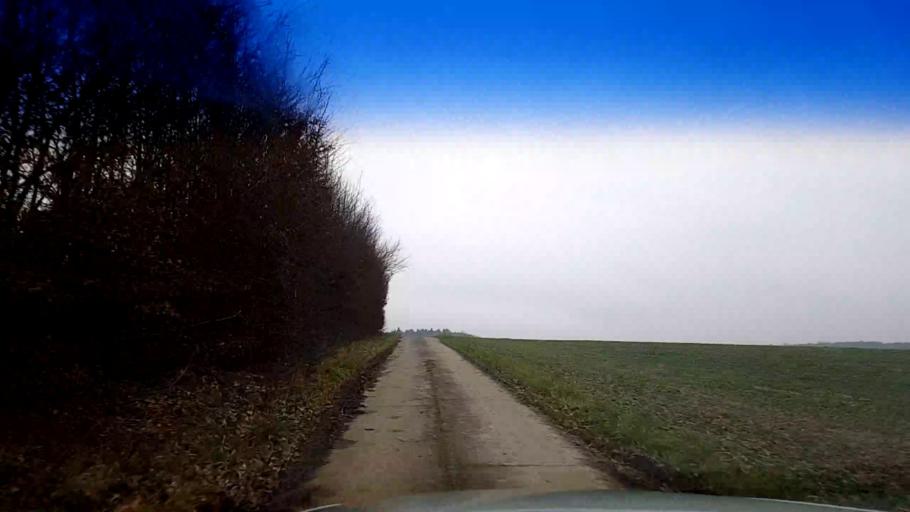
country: DE
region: Bavaria
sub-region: Upper Franconia
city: Memmelsdorf
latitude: 49.9739
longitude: 10.9790
